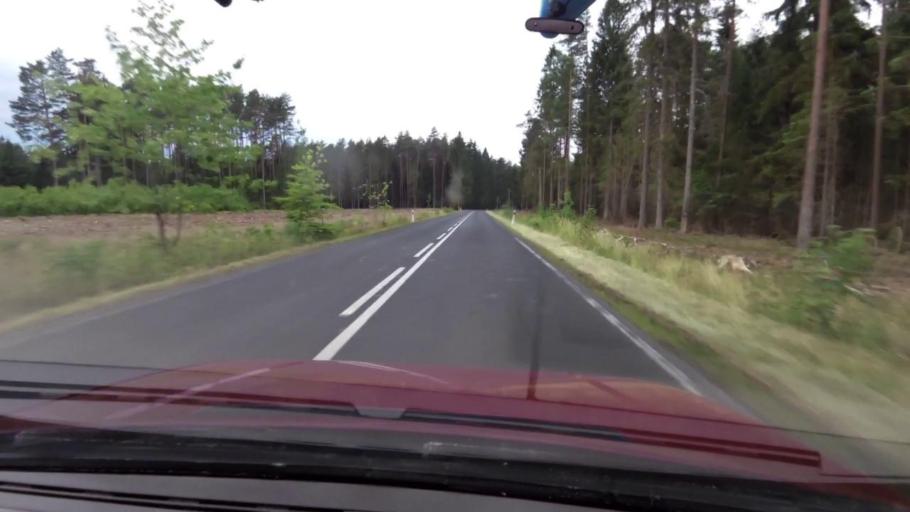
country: PL
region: West Pomeranian Voivodeship
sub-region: Powiat koszalinski
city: Polanow
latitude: 54.1388
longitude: 16.4965
